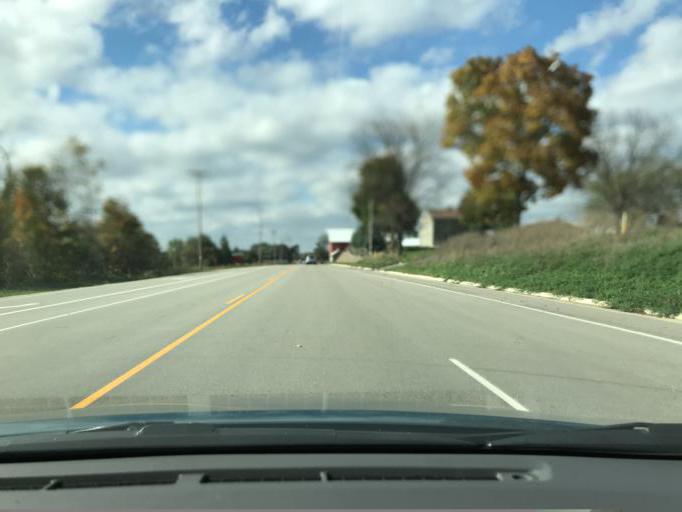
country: US
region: Wisconsin
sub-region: Racine County
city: Browns Lake
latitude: 42.6548
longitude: -88.2219
